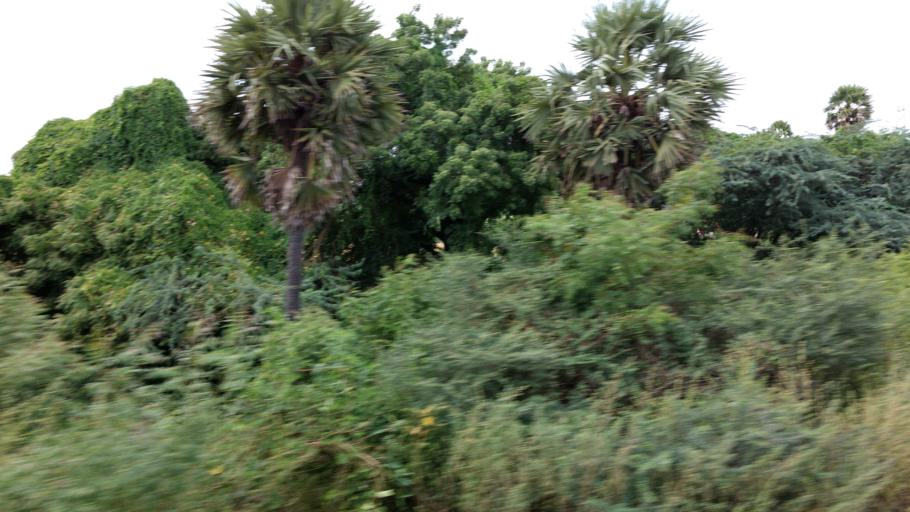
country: IN
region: Tamil Nadu
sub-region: Vellore
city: Gudiyatham
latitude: 12.9199
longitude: 78.8786
